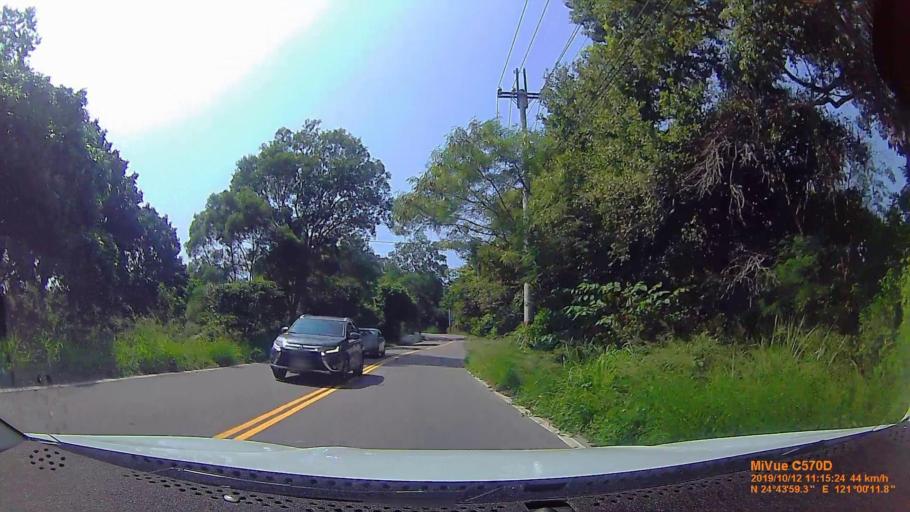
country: TW
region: Taiwan
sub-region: Hsinchu
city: Hsinchu
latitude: 24.7330
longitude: 121.0032
